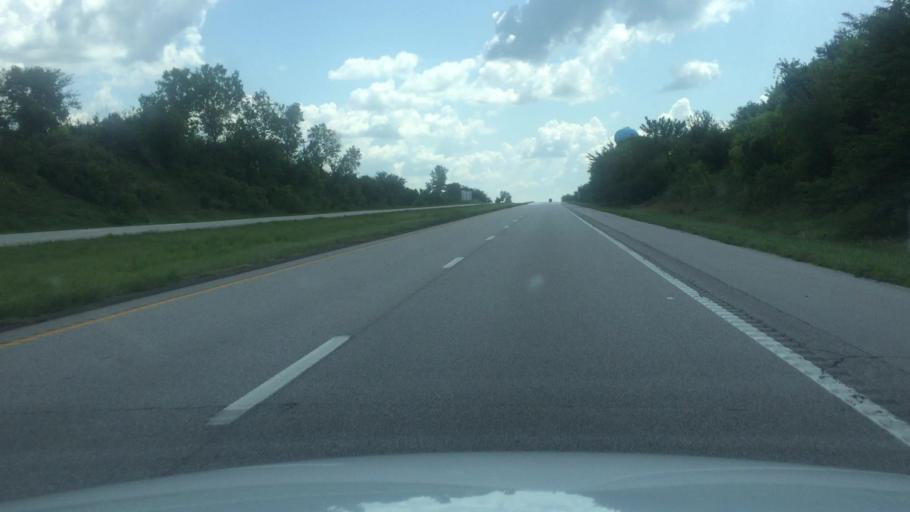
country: US
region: Missouri
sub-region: Platte County
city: Platte City
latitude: 39.3264
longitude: -94.7551
